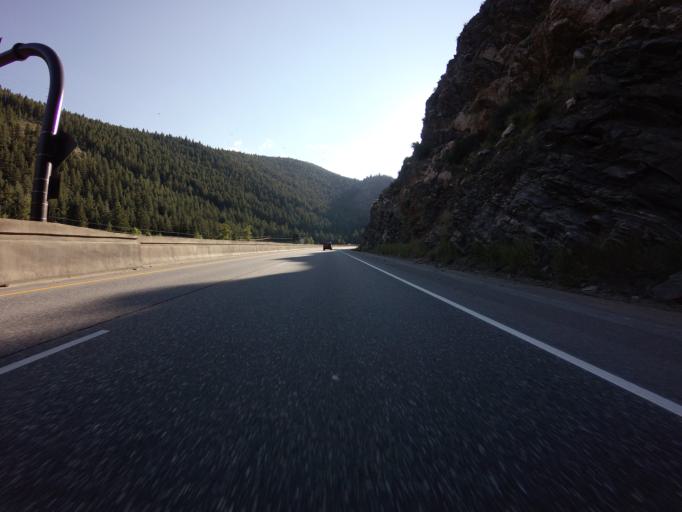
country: US
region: Colorado
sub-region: Clear Creek County
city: Idaho Springs
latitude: 39.7438
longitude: -105.4506
